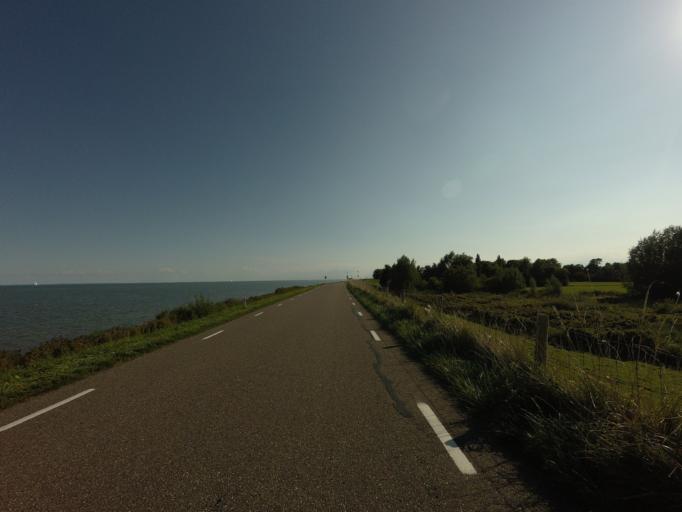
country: NL
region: North Holland
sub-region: Gemeente Enkhuizen
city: Enkhuizen
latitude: 52.6805
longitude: 5.2433
